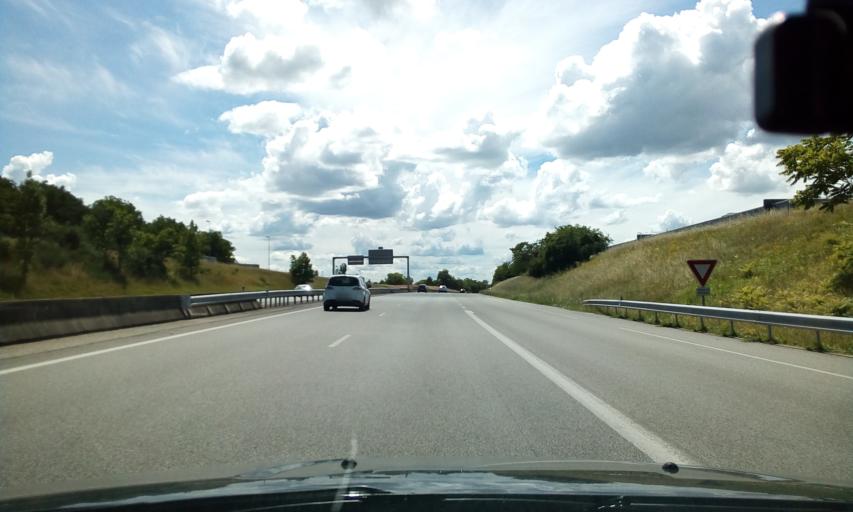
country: FR
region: Rhone-Alpes
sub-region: Departement de l'Isere
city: Saint-Marcellin
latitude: 45.1349
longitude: 5.3225
